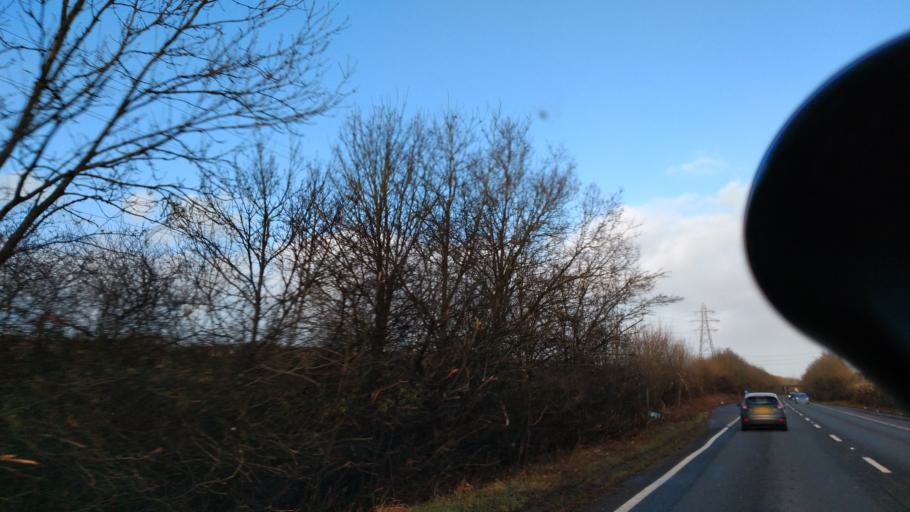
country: GB
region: England
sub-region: Somerset
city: Frome
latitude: 51.2336
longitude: -2.2959
